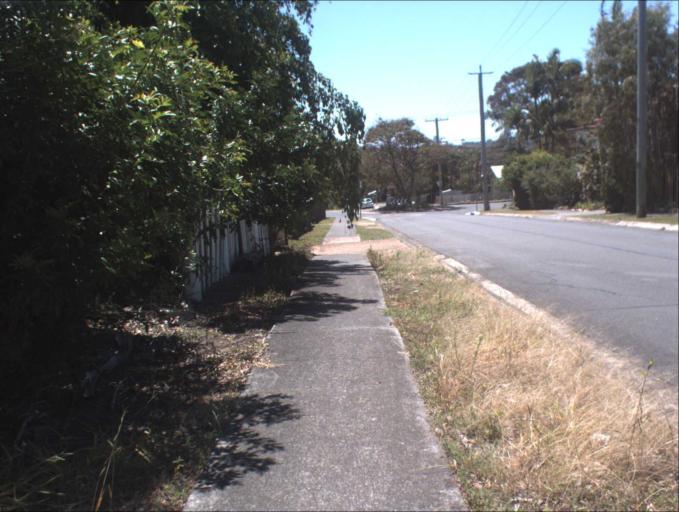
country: AU
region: Queensland
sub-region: Logan
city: Logan City
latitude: -27.6375
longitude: 153.1159
